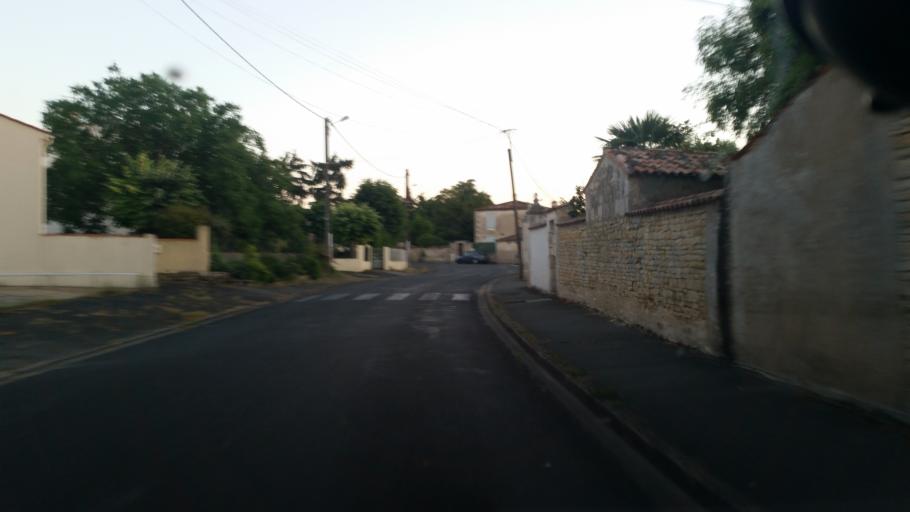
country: FR
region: Poitou-Charentes
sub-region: Departement de la Charente-Maritime
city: Marans
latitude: 46.3085
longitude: -0.9994
